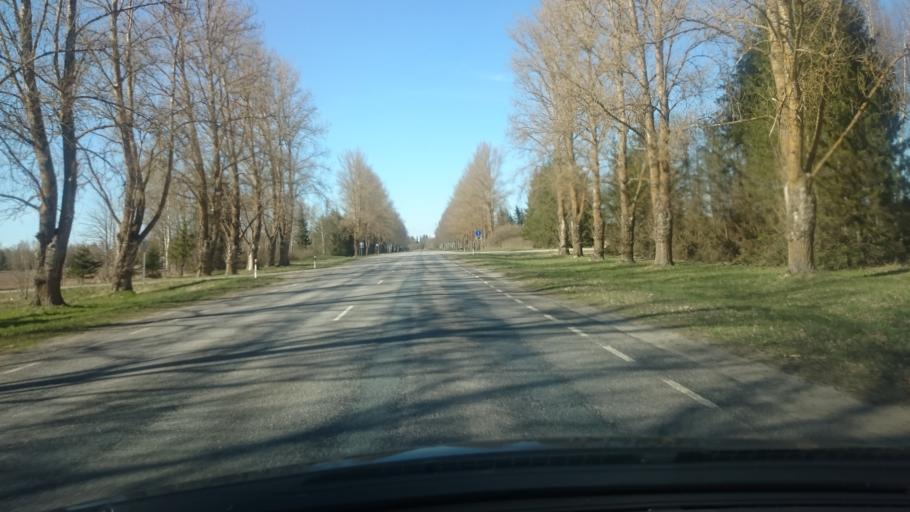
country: EE
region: Polvamaa
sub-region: Polva linn
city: Polva
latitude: 58.2977
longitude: 27.0014
